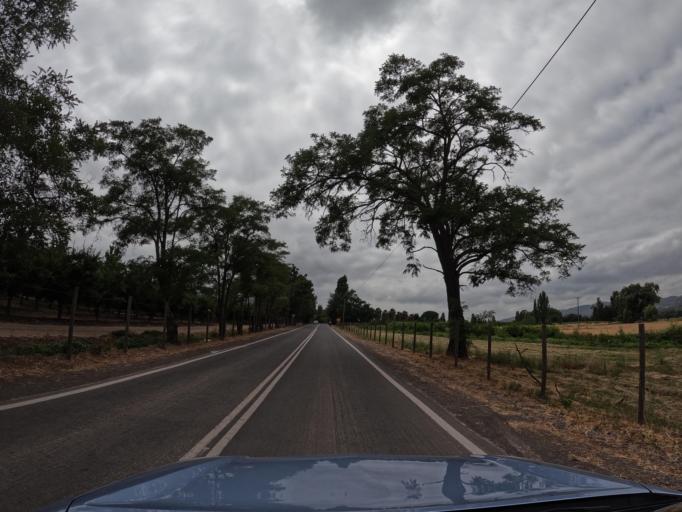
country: CL
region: Maule
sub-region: Provincia de Curico
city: Teno
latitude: -34.7584
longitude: -71.2116
